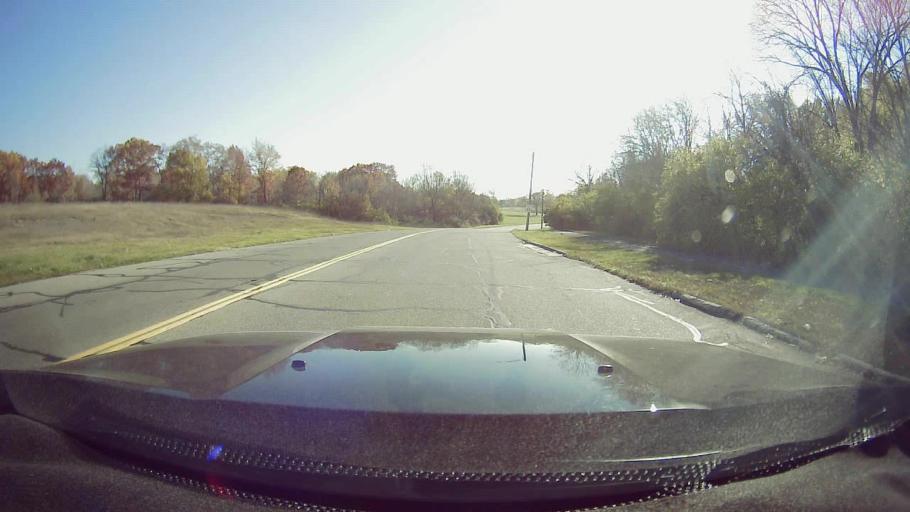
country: US
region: Michigan
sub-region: Wayne County
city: Dearborn Heights
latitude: 42.3520
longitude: -83.2492
